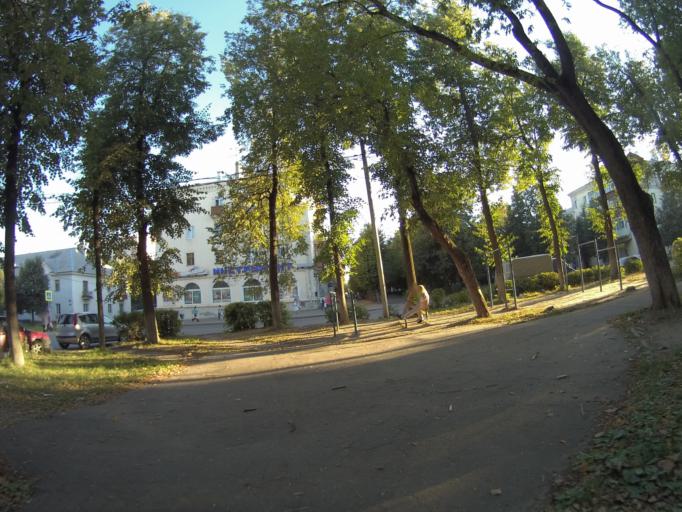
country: RU
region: Vladimir
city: Vladimir
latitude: 56.1486
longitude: 40.3834
